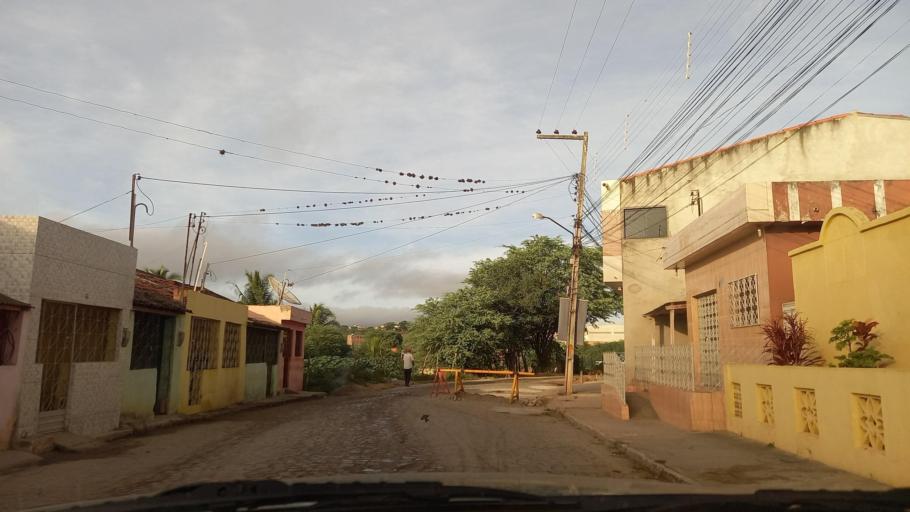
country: BR
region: Pernambuco
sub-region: Bezerros
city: Bezerros
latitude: -8.2240
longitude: -35.7496
